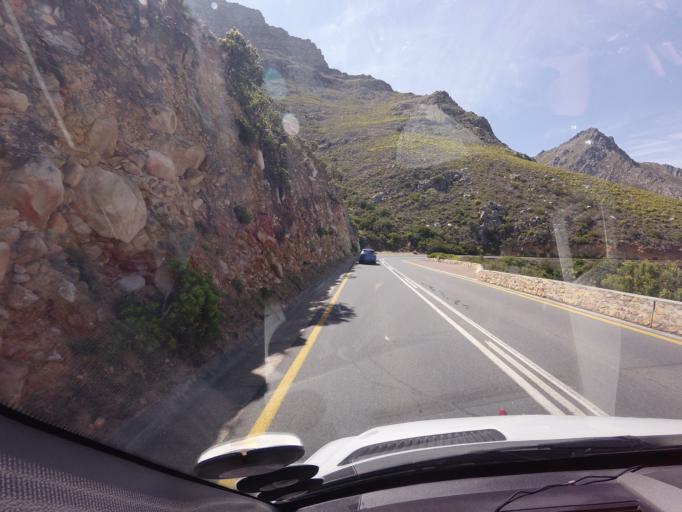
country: ZA
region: Western Cape
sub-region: Overberg District Municipality
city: Grabouw
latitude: -34.2082
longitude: 18.8333
